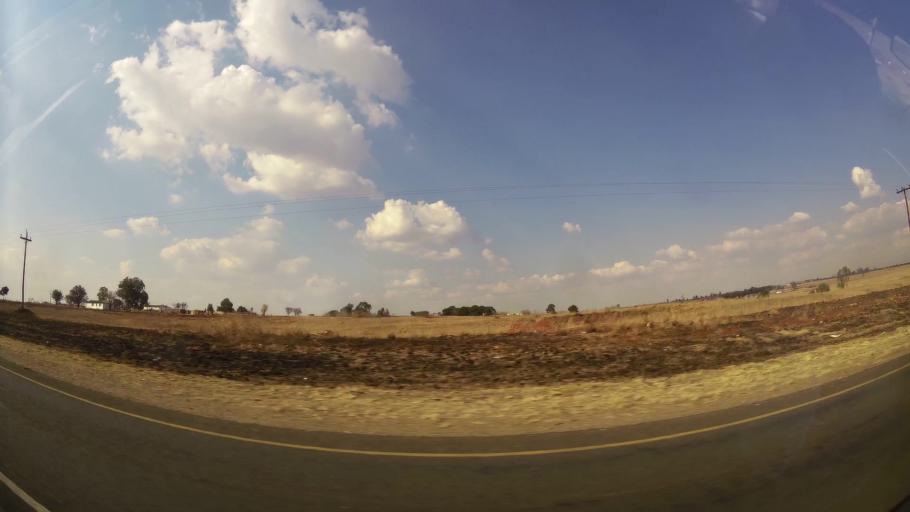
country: ZA
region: Gauteng
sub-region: Ekurhuleni Metropolitan Municipality
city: Brakpan
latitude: -26.3208
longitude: 28.3382
